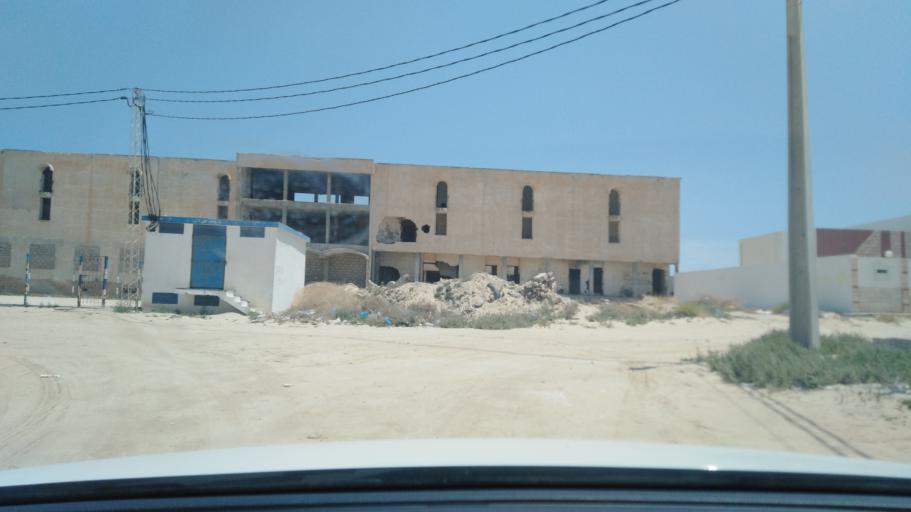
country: TN
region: Qabis
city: Gabes
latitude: 33.9489
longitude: 10.0729
